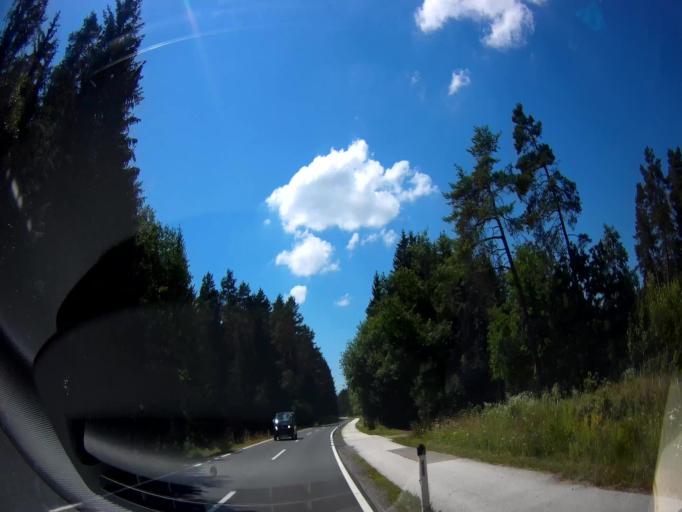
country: AT
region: Carinthia
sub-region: Politischer Bezirk Volkermarkt
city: Globasnitz
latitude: 46.6027
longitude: 14.7361
